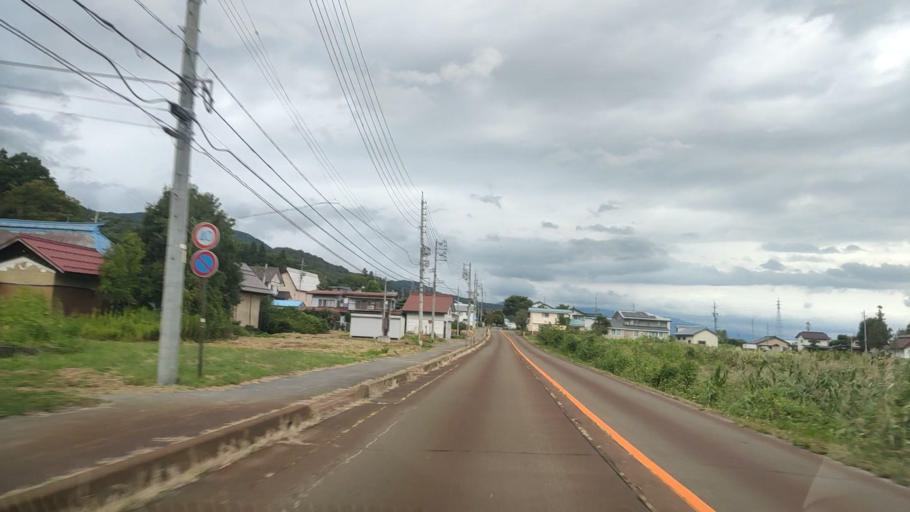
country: JP
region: Nagano
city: Iiyama
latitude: 36.8134
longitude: 138.3492
